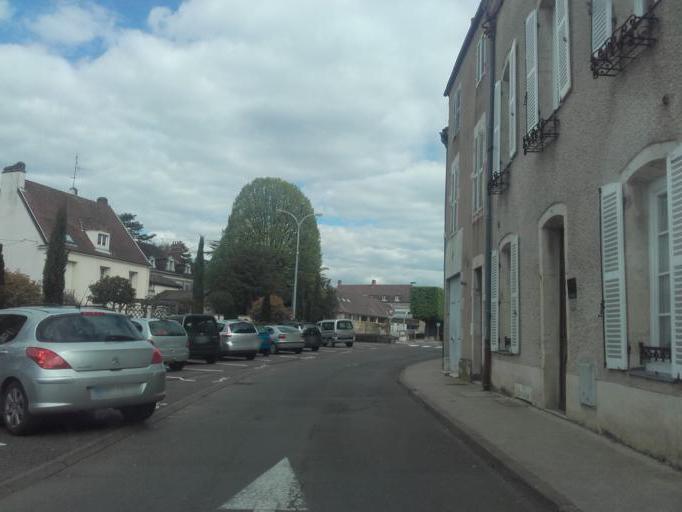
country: FR
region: Bourgogne
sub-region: Departement de la Cote-d'Or
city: Nuits-Saint-Georges
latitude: 47.1356
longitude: 4.9472
